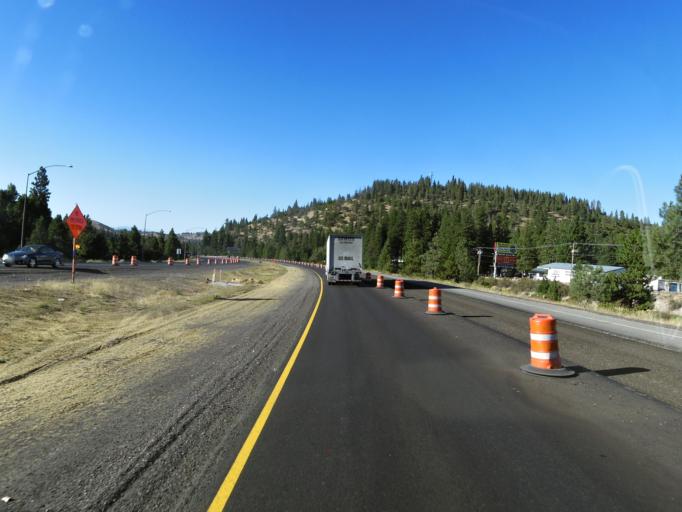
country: US
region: California
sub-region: Siskiyou County
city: Weed
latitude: 41.4095
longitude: -122.3798
